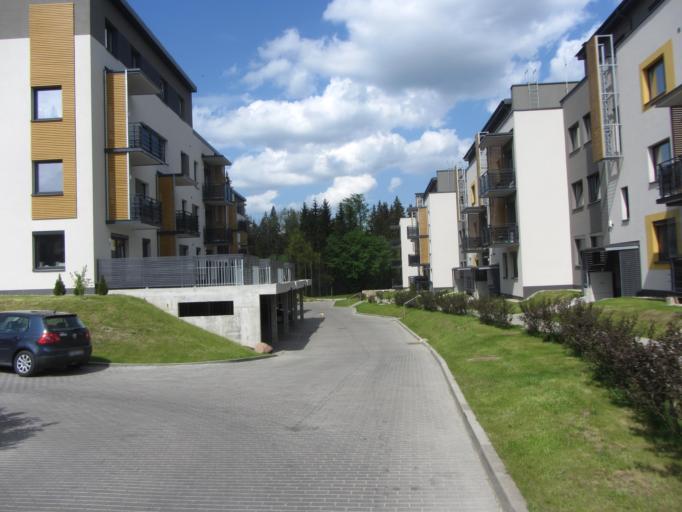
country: LT
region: Vilnius County
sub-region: Vilnius
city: Fabijoniskes
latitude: 54.7649
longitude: 25.2841
